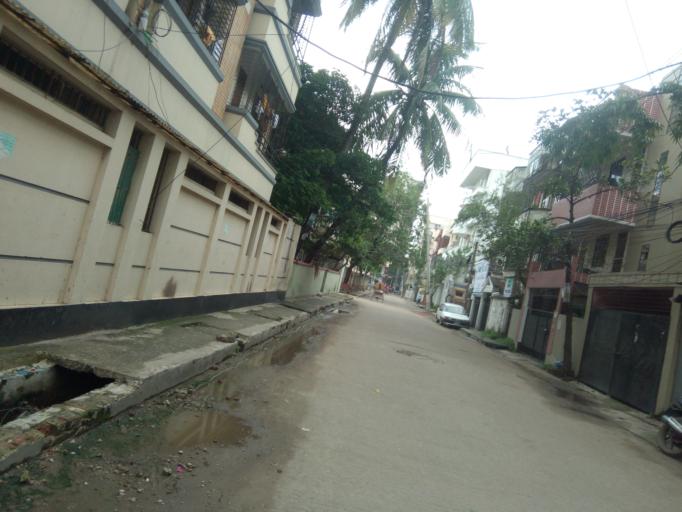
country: BD
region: Dhaka
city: Azimpur
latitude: 23.7694
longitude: 90.3665
